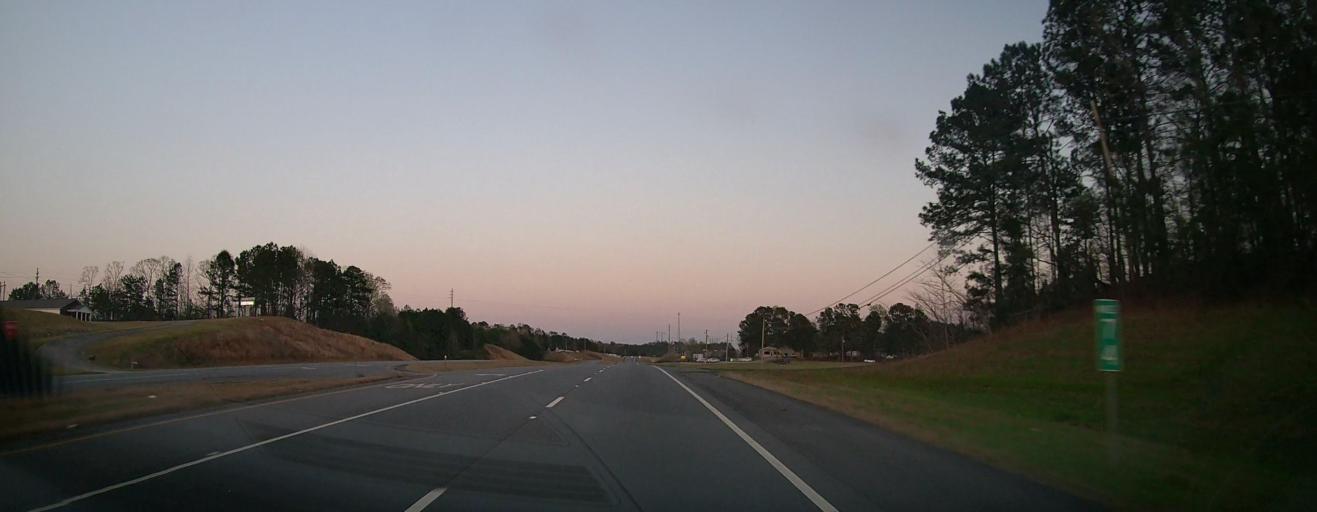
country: US
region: Alabama
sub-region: Tallapoosa County
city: Alexander City
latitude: 32.8858
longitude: -85.8679
